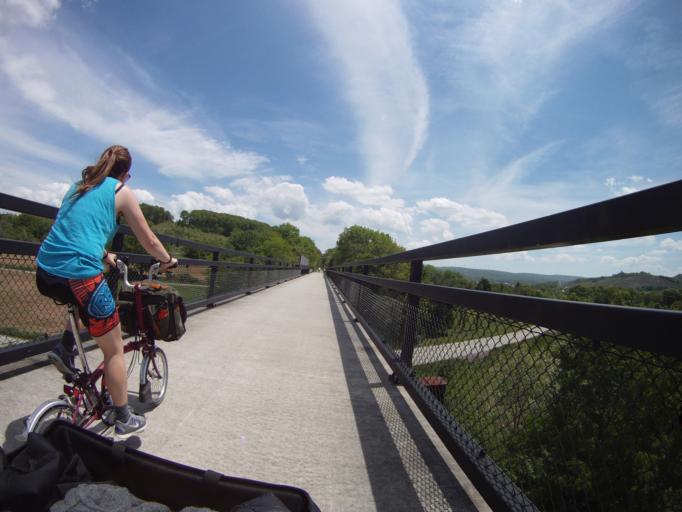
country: US
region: Pennsylvania
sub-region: Somerset County
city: Meyersdale
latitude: 39.8327
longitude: -79.0425
